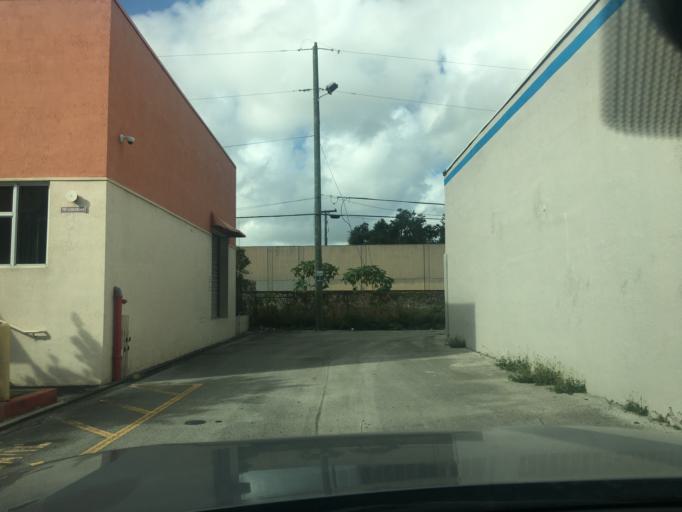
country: US
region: Florida
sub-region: Broward County
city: Pembroke Park
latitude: 25.9812
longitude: -80.1663
